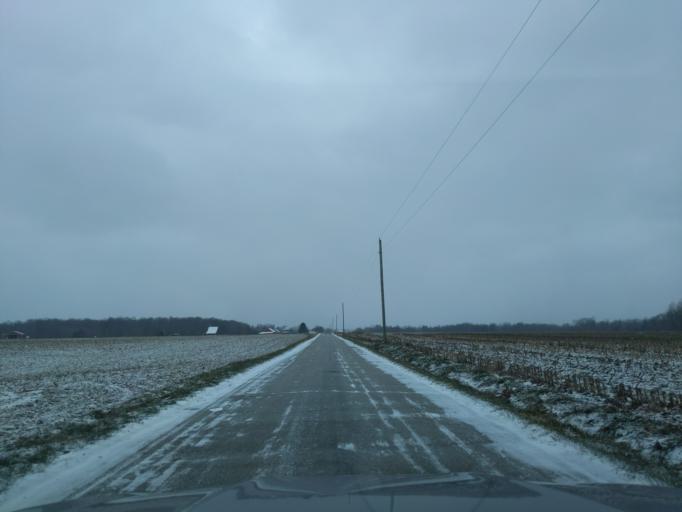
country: US
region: Indiana
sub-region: Decatur County
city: Westport
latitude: 39.2290
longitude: -85.4967
